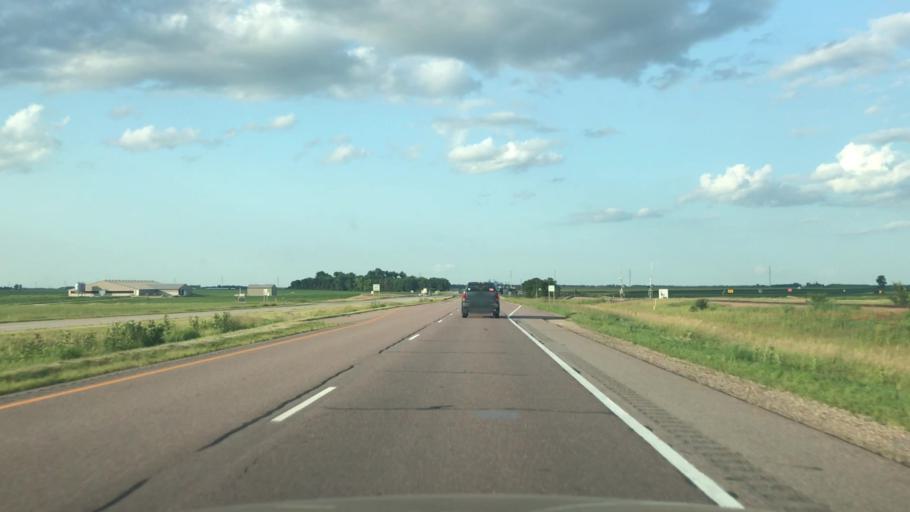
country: US
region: Minnesota
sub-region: Nobles County
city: Worthington
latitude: 43.6592
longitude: -95.5321
